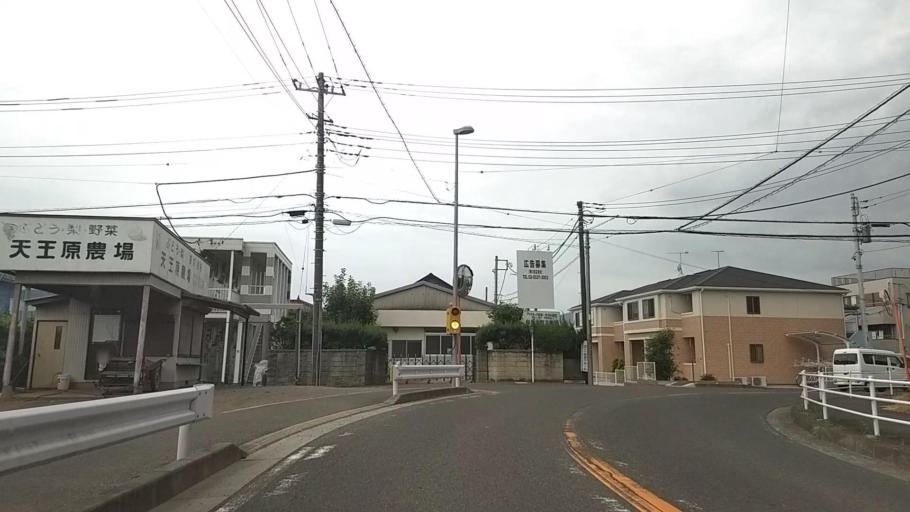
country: JP
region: Kanagawa
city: Isehara
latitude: 35.3913
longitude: 139.3224
